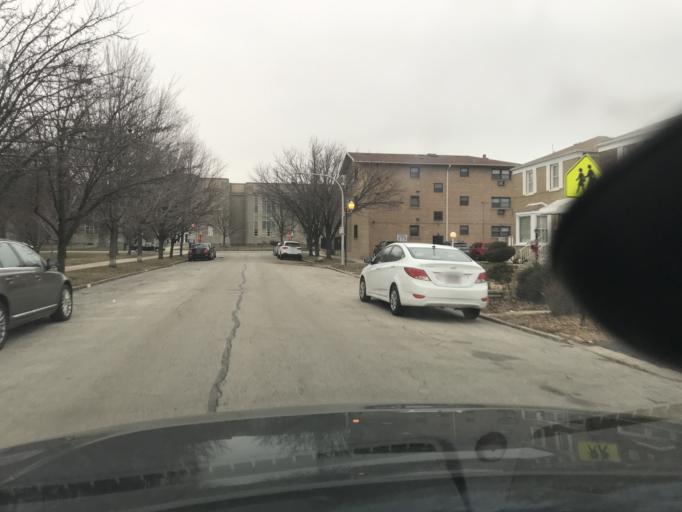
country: US
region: Indiana
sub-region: Lake County
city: Whiting
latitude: 41.7362
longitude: -87.5733
